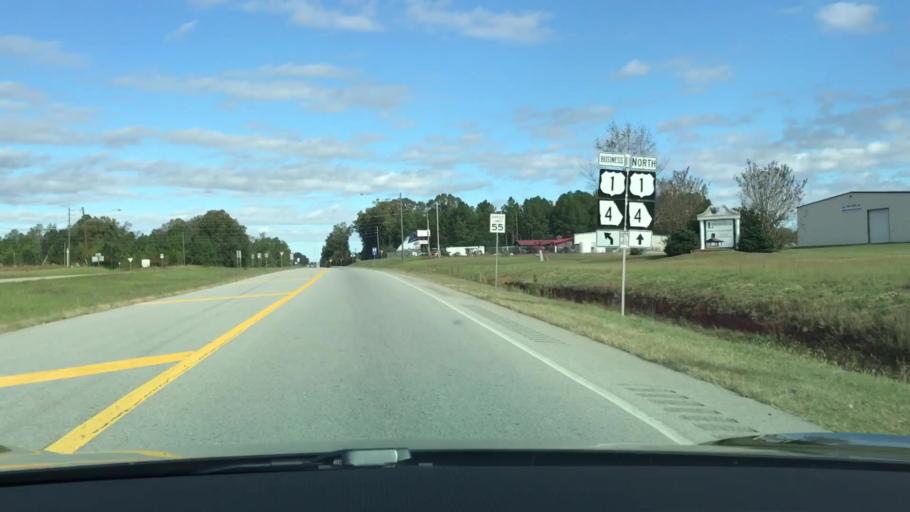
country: US
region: Georgia
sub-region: Jefferson County
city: Louisville
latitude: 32.9839
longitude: -82.3919
